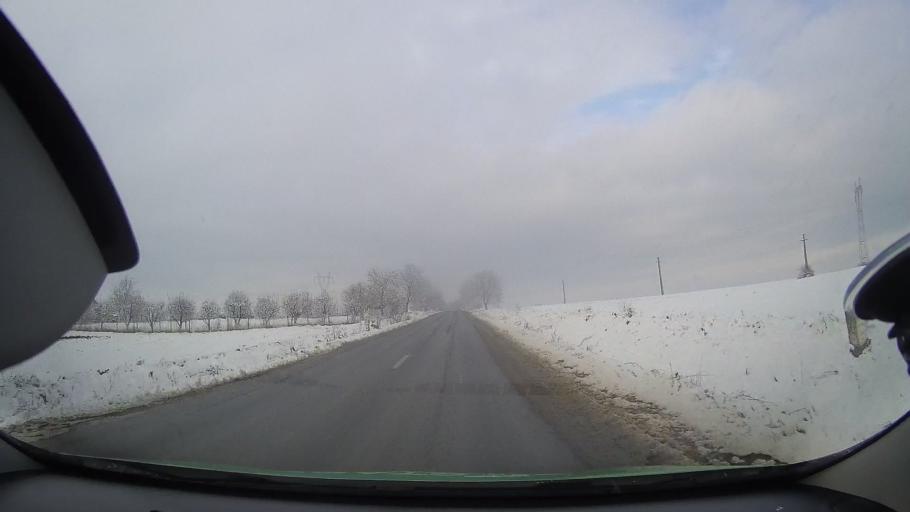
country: RO
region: Mures
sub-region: Comuna Atintis
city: Atintis
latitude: 46.4401
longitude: 24.0923
